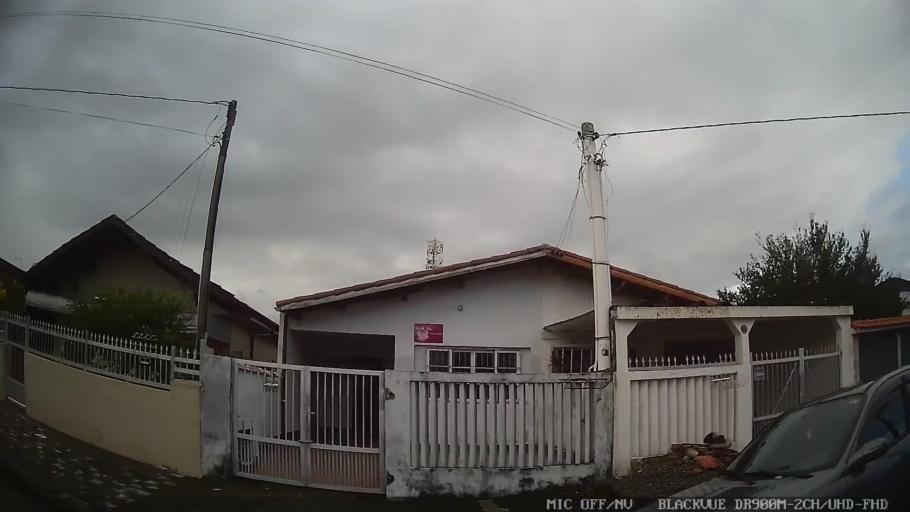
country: BR
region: Sao Paulo
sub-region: Itanhaem
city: Itanhaem
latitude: -24.1793
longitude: -46.7908
